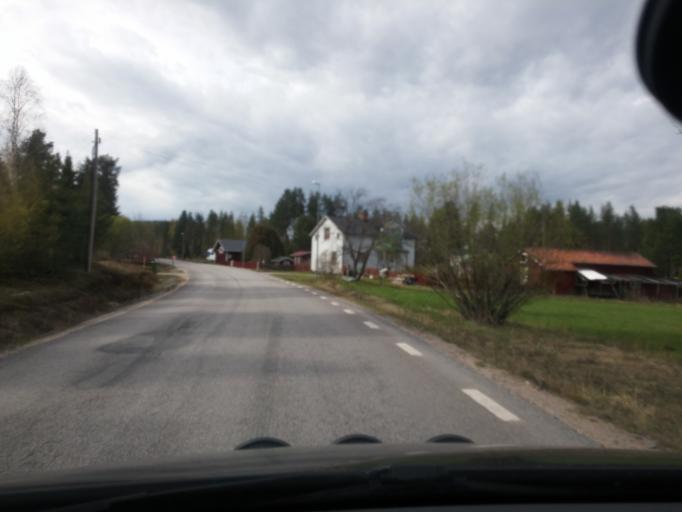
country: SE
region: Gaevleborg
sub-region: Ljusdals Kommun
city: Farila
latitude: 61.7983
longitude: 15.9097
